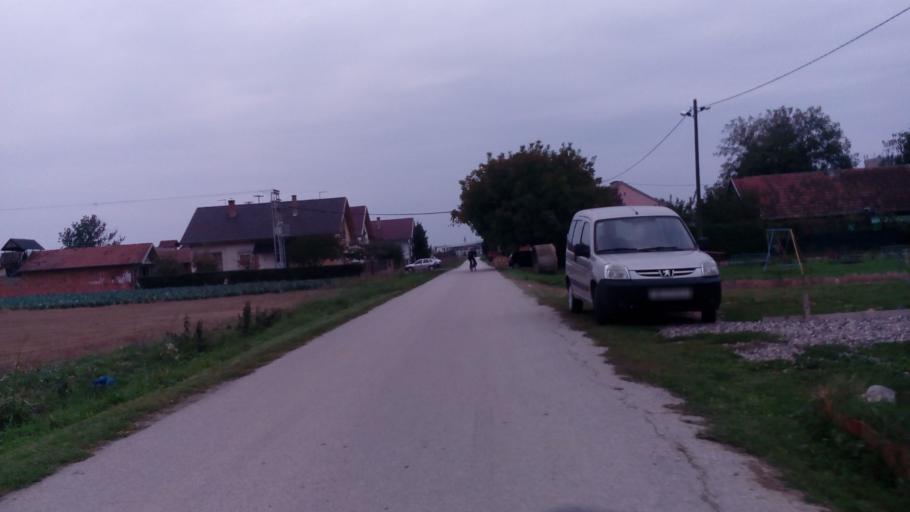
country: HR
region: Vukovarsko-Srijemska
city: Vinkovci
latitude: 45.2690
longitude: 18.8138
